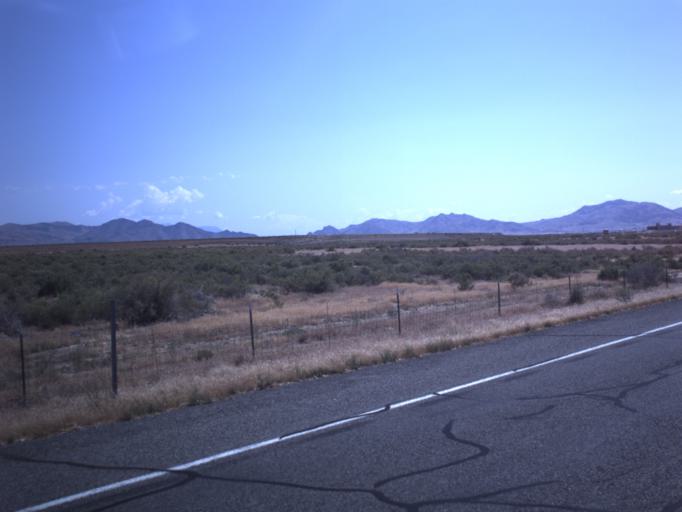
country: US
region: Utah
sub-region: Millard County
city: Delta
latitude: 39.4684
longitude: -112.4517
